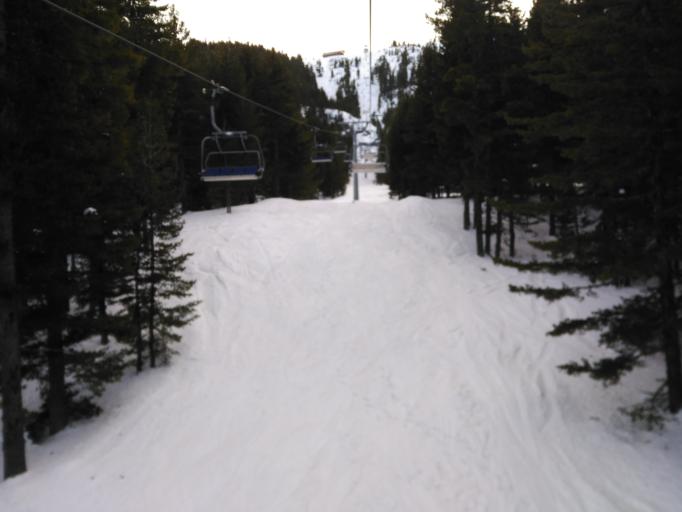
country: BG
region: Blagoevgrad
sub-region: Obshtina Bansko
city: Bansko
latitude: 41.7694
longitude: 23.4483
